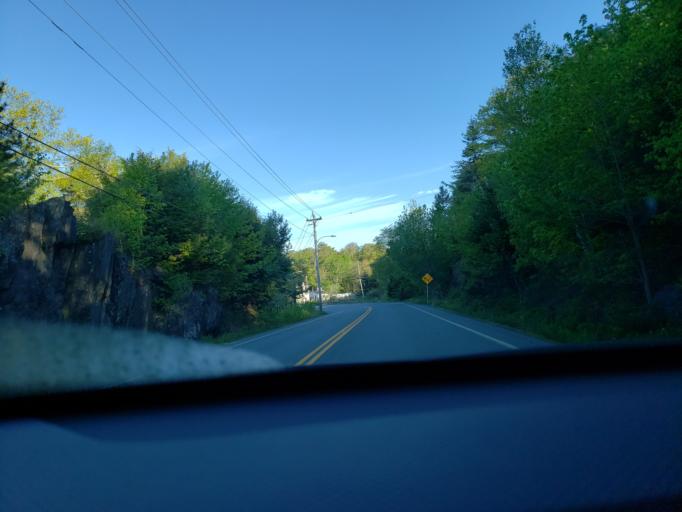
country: CA
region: Nova Scotia
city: Cole Harbour
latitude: 44.7397
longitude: -63.3830
